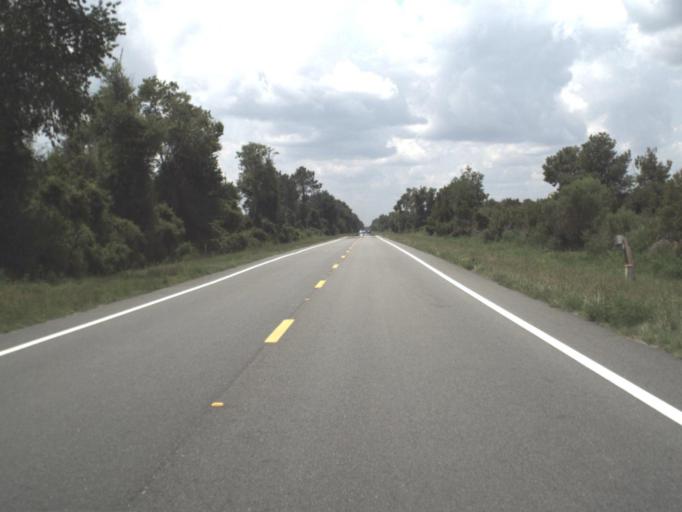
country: US
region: Florida
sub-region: Hamilton County
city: Jasper
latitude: 30.4516
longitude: -82.8876
